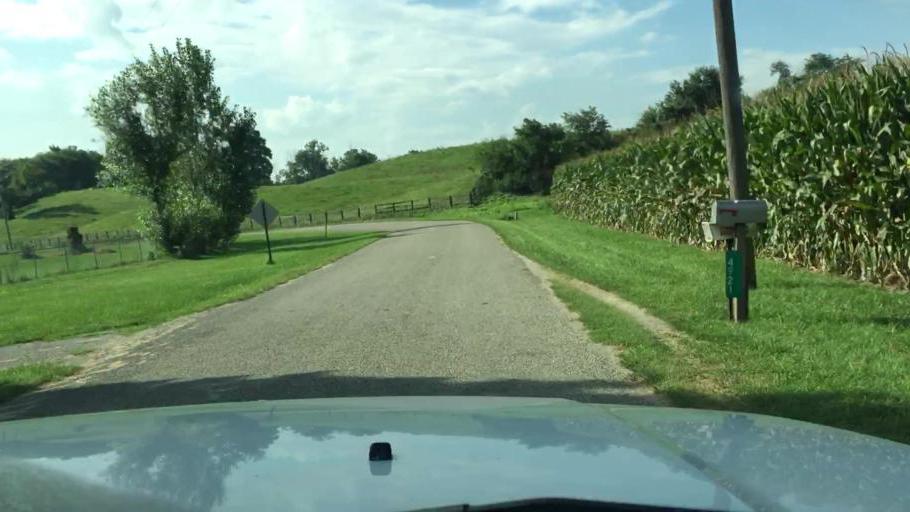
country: US
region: Ohio
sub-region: Champaign County
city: Mechanicsburg
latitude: 40.0604
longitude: -83.6007
